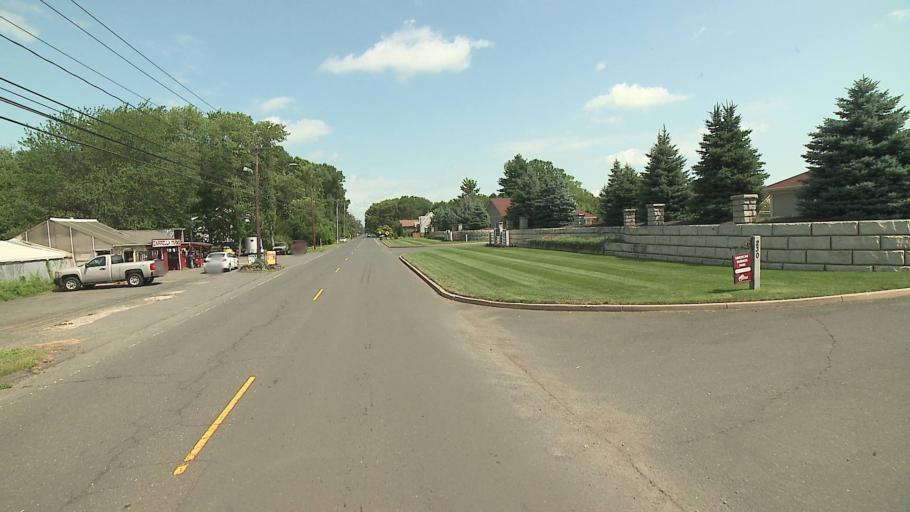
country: US
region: Connecticut
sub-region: Hartford County
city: Plainville
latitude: 41.6566
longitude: -72.8749
